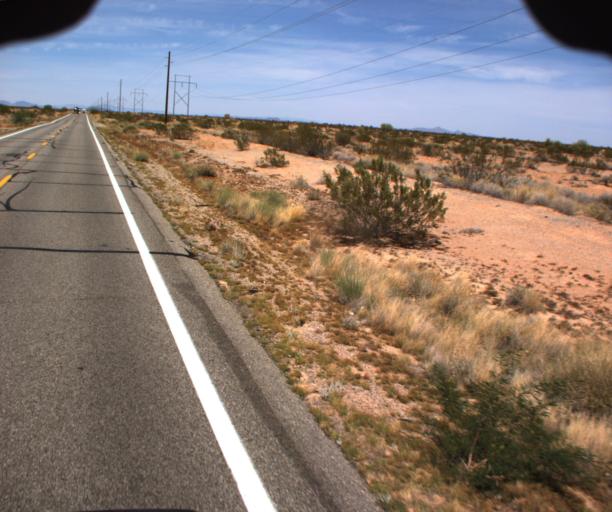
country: US
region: Arizona
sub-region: La Paz County
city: Quartzsite
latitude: 33.8549
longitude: -114.2169
